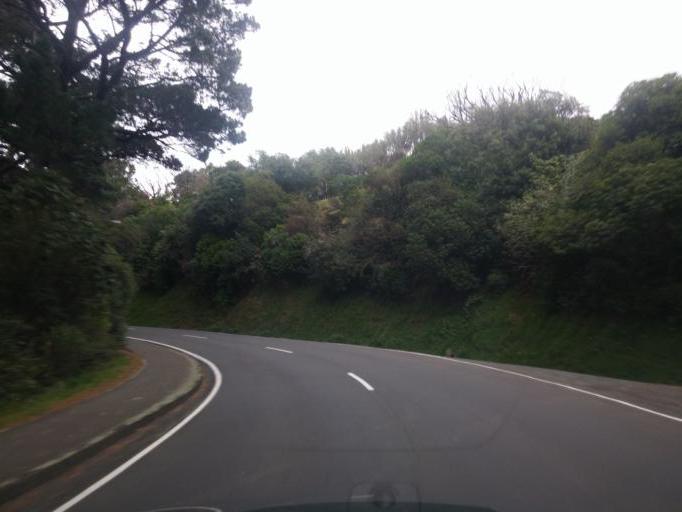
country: NZ
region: Wellington
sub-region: Wellington City
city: Wellington
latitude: -41.2997
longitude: 174.7659
